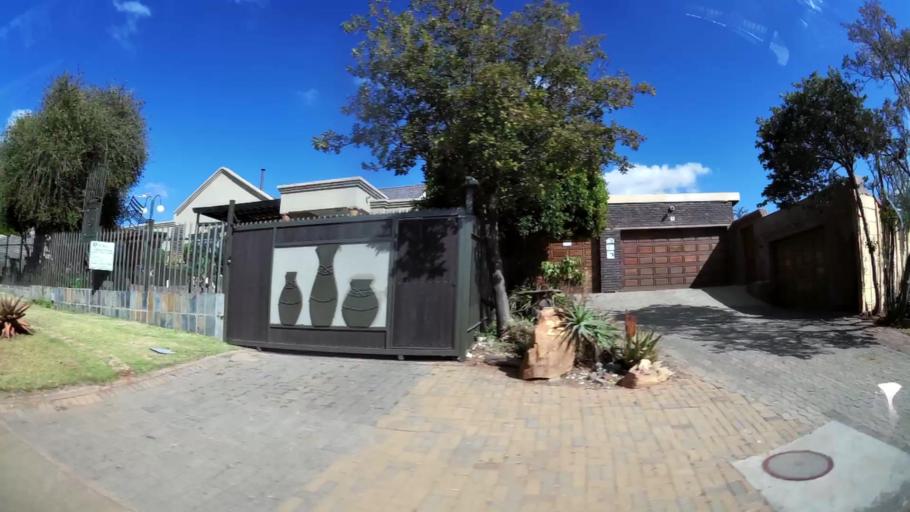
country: ZA
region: Gauteng
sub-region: West Rand District Municipality
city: Krugersdorp
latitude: -26.1203
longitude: 27.8229
